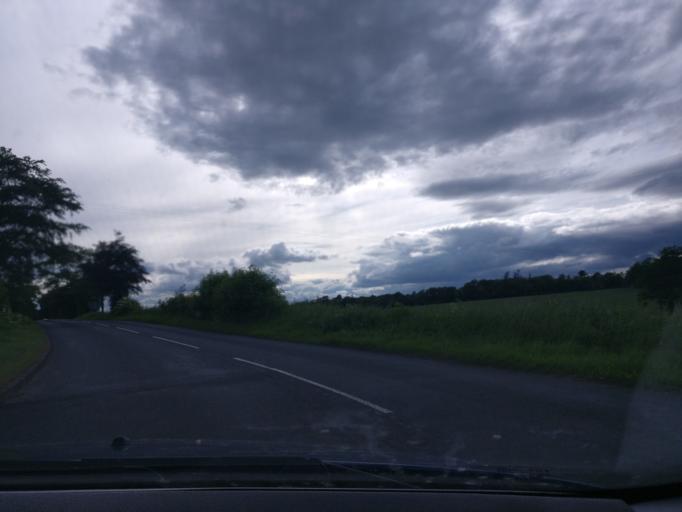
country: GB
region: Scotland
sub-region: East Lothian
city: Haddington
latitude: 55.9385
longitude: -2.7530
